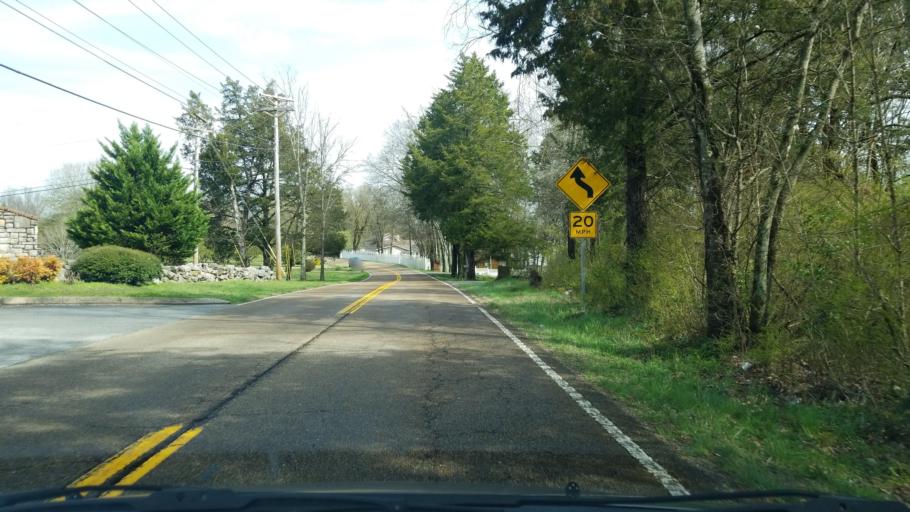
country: US
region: Tennessee
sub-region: Hamilton County
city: Harrison
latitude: 35.1485
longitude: -85.0616
